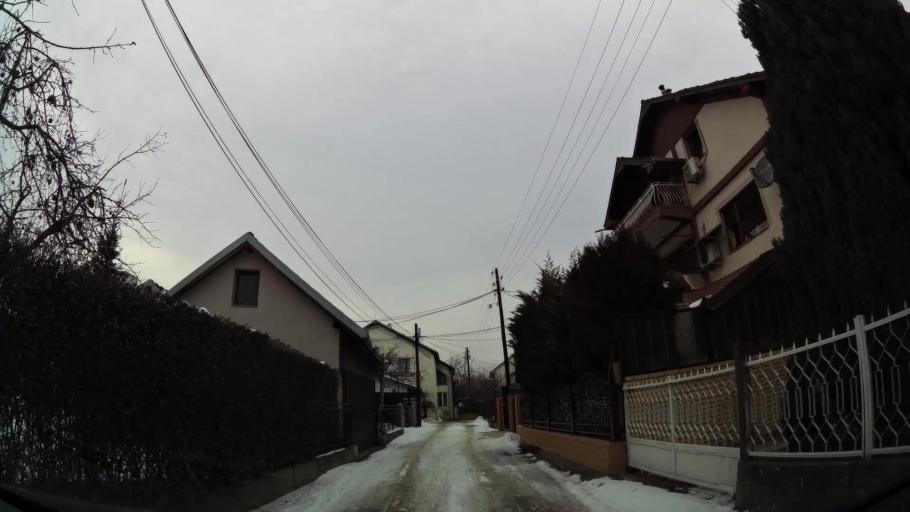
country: MK
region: Butel
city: Butel
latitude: 42.0379
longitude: 21.4481
